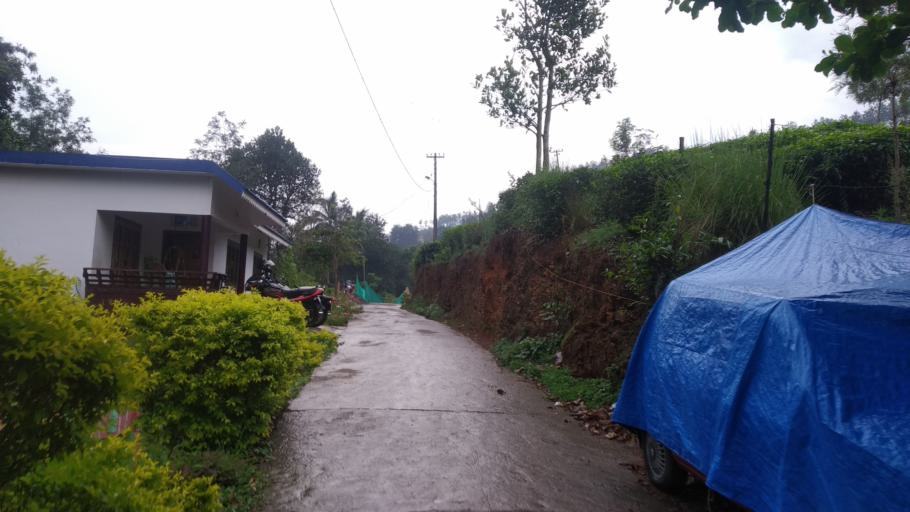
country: IN
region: Tamil Nadu
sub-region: Theni
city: Gudalur
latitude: 9.5686
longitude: 77.0897
